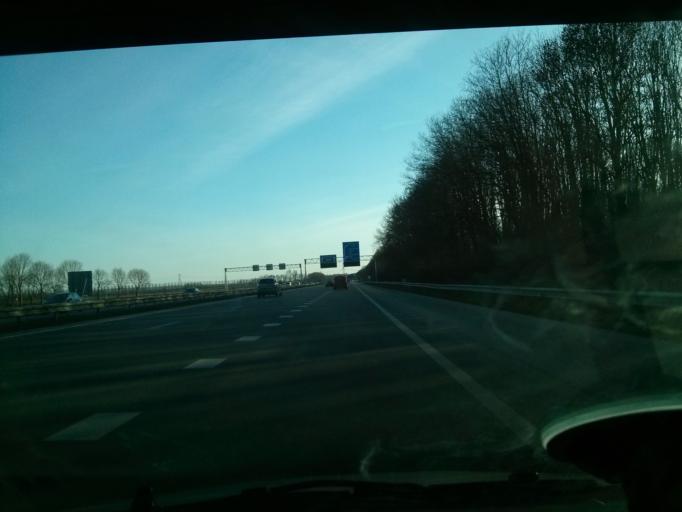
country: NL
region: Gelderland
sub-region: Gemeente Overbetuwe
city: Elst
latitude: 51.9144
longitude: 5.8739
